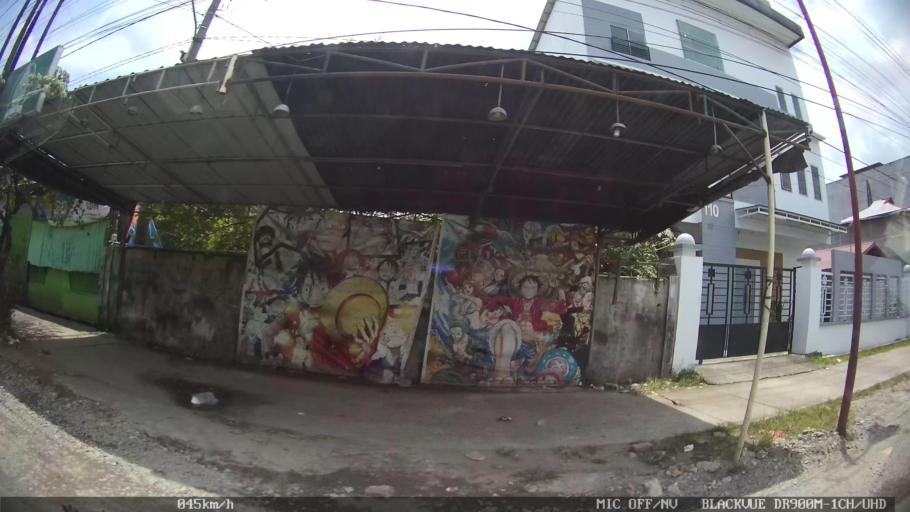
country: ID
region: North Sumatra
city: Medan
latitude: 3.6164
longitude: 98.6894
